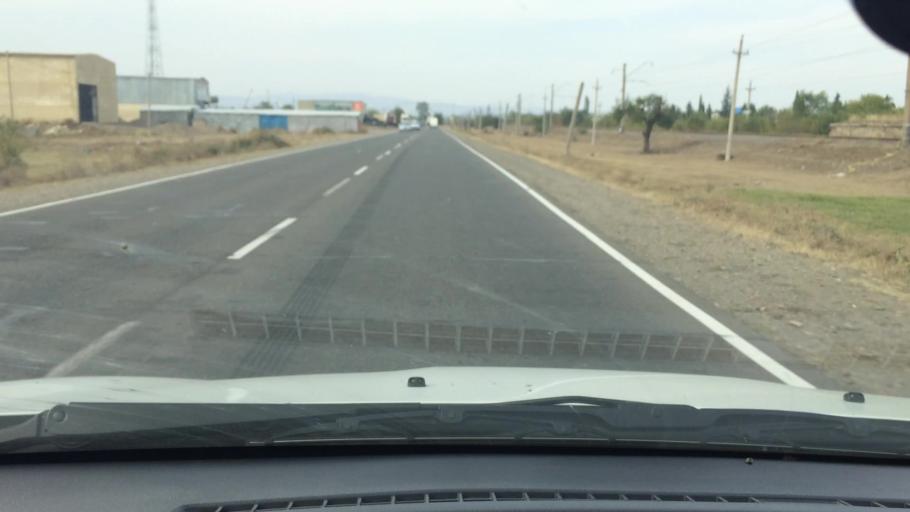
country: GE
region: Kvemo Kartli
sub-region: Marneuli
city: Marneuli
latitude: 41.4343
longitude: 44.8198
